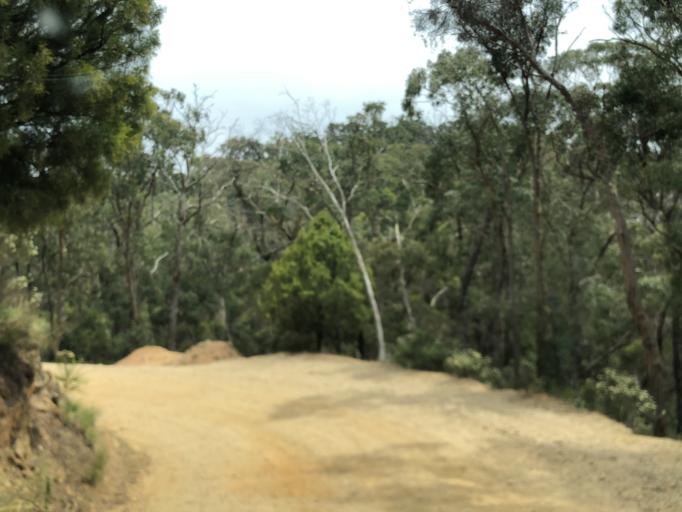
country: AU
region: Victoria
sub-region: Moorabool
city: Bacchus Marsh
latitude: -37.4951
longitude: 144.3600
